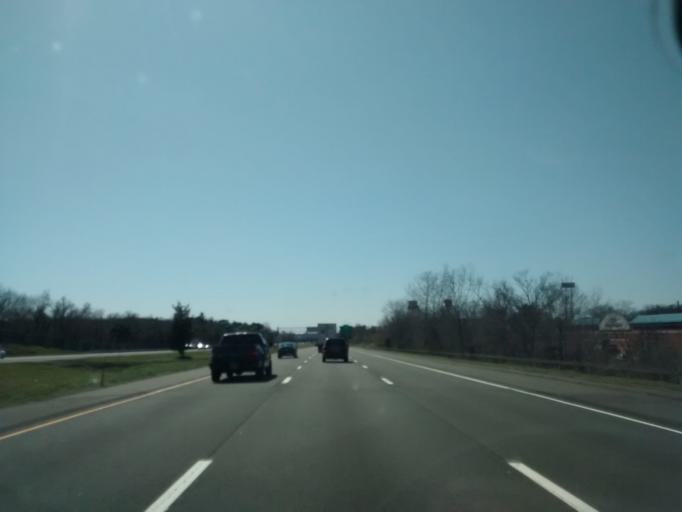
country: US
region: Connecticut
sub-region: Tolland County
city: Rockville
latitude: 41.8293
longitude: -72.4761
